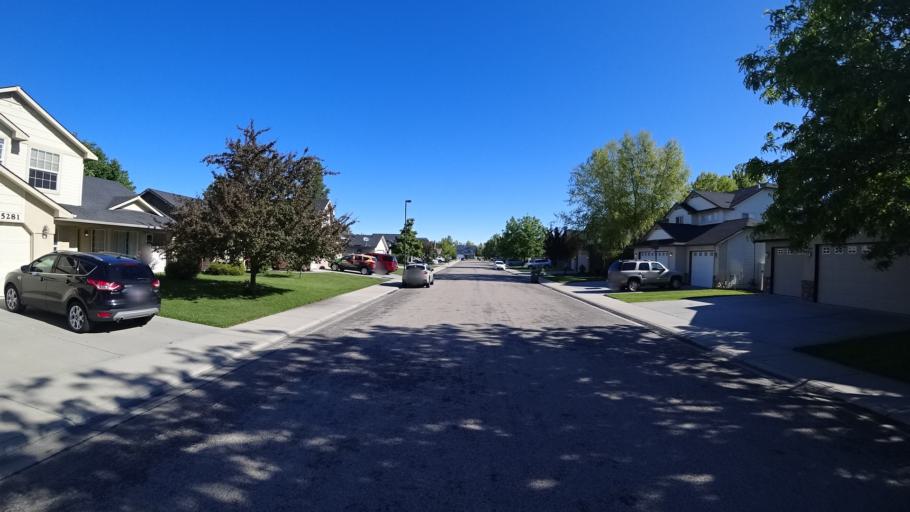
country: US
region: Idaho
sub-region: Ada County
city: Meridian
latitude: 43.6527
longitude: -116.4291
